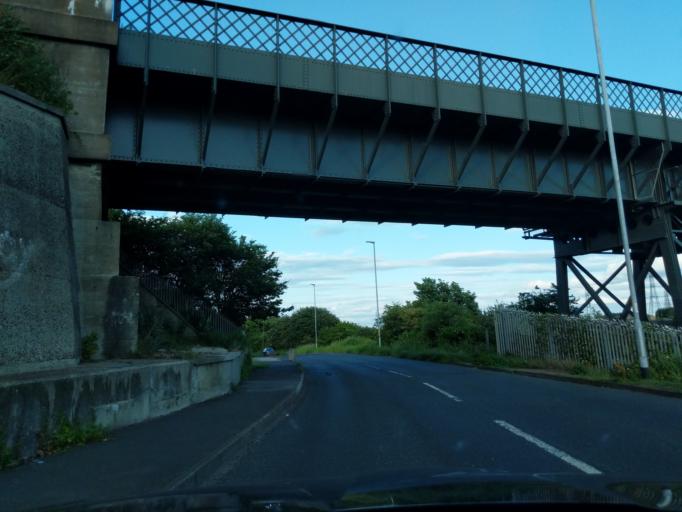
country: GB
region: England
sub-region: Northumberland
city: Bedlington
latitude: 55.1350
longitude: -1.5639
